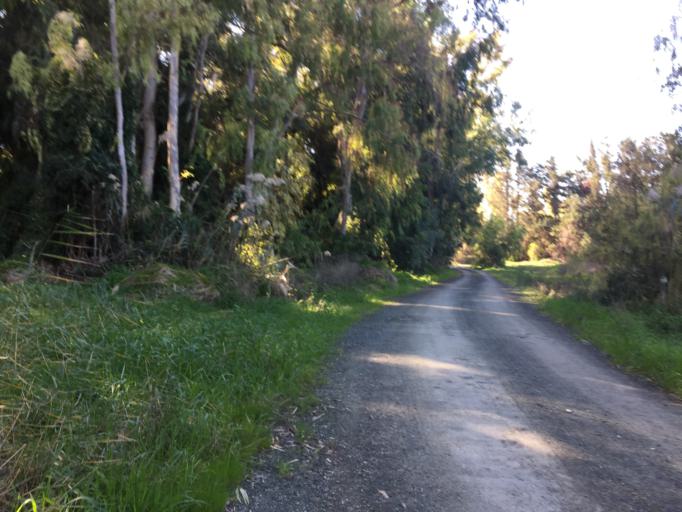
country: CY
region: Larnaka
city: Kolossi
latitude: 34.6288
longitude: 32.9587
